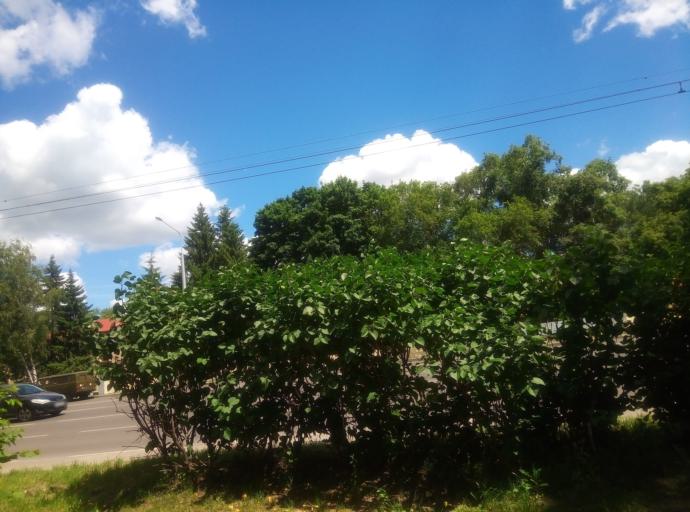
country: RU
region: Kursk
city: Kursk
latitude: 51.7639
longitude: 36.1843
